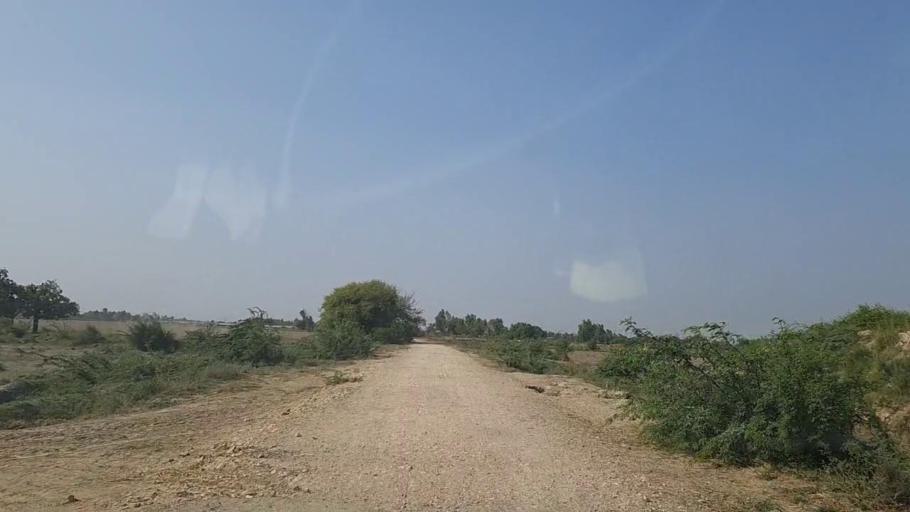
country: PK
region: Sindh
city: Mirpur Sakro
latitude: 24.5636
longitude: 67.8290
